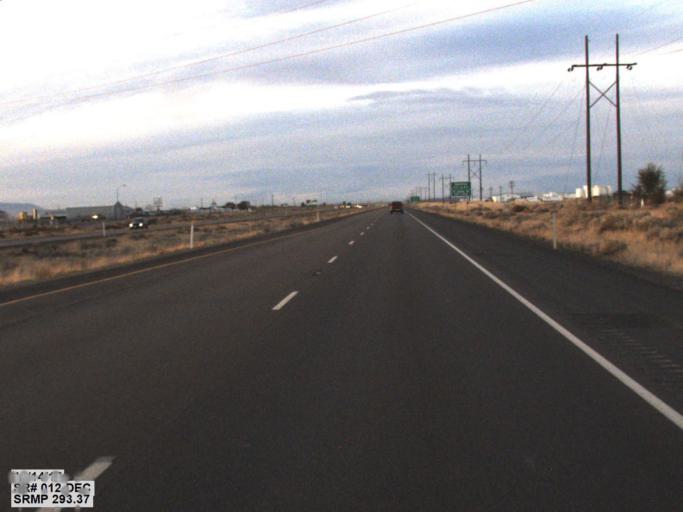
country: US
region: Washington
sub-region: Walla Walla County
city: Burbank
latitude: 46.2296
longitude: -119.0423
